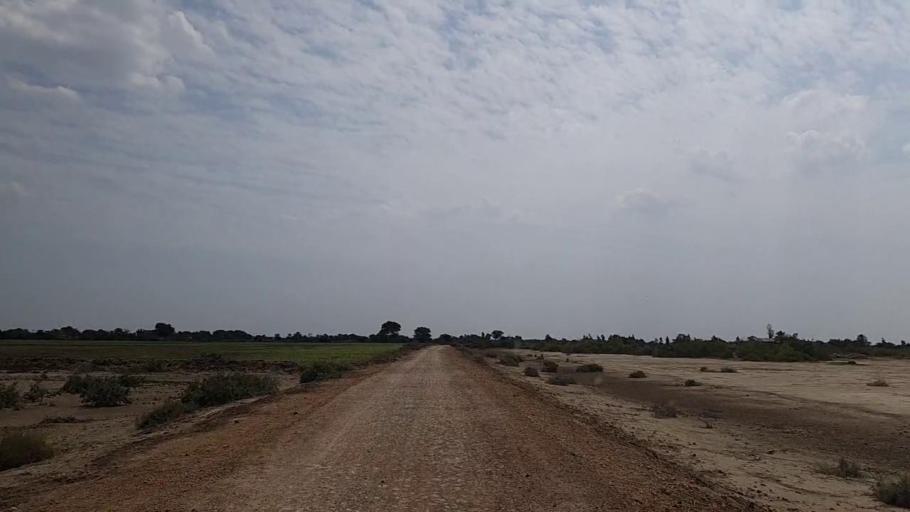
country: PK
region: Sindh
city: Daro Mehar
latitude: 24.8332
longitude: 68.1643
